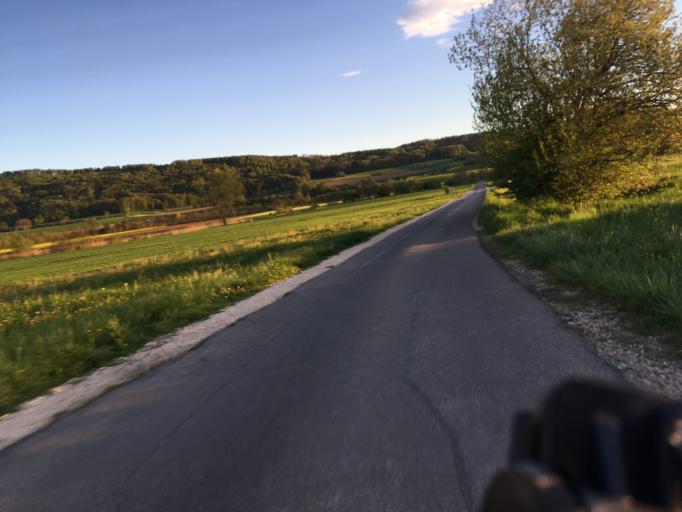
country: DE
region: Baden-Wuerttemberg
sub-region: Freiburg Region
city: Gottmadingen
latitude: 47.7242
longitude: 8.7750
